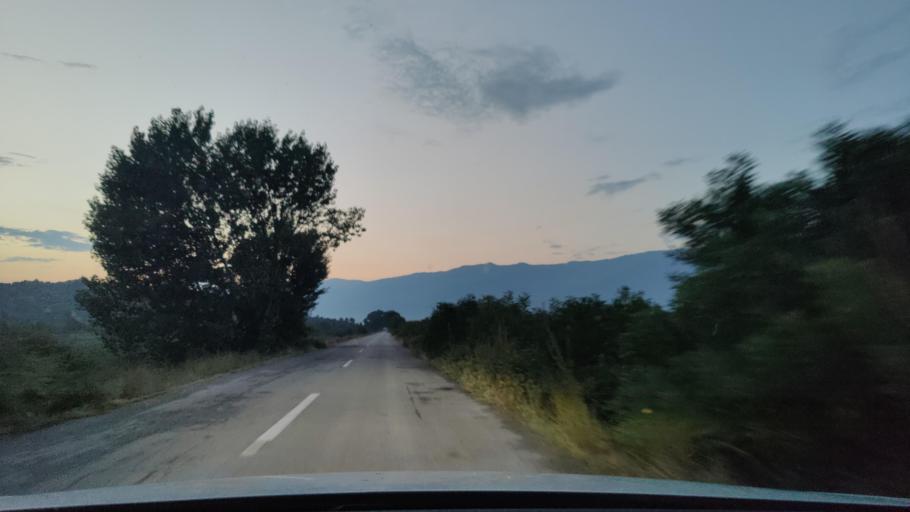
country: GR
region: Central Macedonia
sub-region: Nomos Serron
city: Chrysochorafa
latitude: 41.1889
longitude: 23.0994
